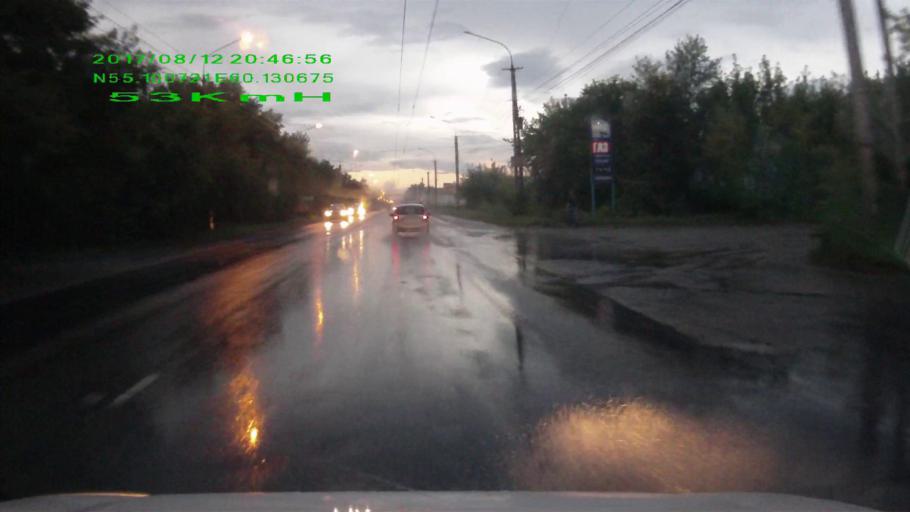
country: RU
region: Chelyabinsk
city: Turgoyak
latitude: 55.1010
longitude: 60.1307
